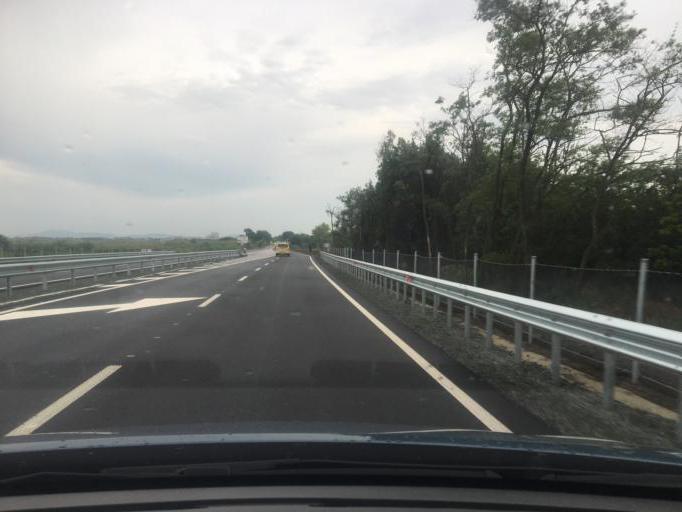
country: BG
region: Burgas
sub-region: Obshtina Pomorie
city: Pomorie
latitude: 42.5964
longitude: 27.6152
